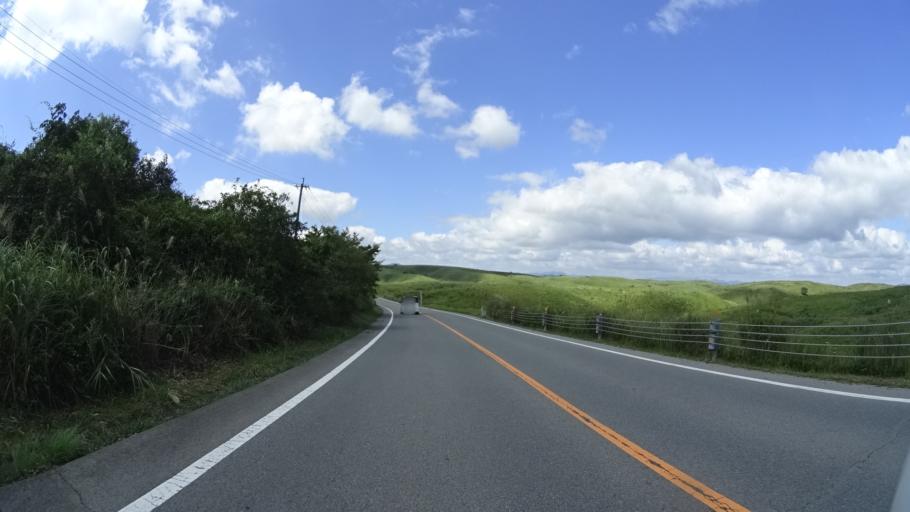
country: JP
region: Kumamoto
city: Aso
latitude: 33.0093
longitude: 131.1148
